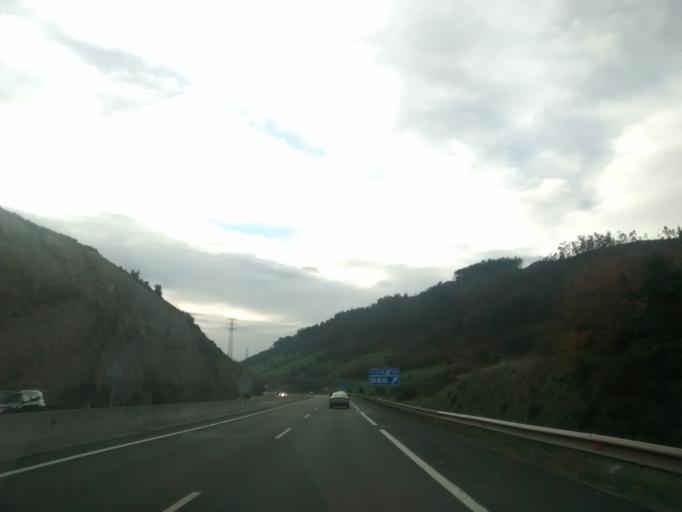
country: ES
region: Cantabria
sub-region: Provincia de Cantabria
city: Castro-Urdiales
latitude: 43.3519
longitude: -3.1677
